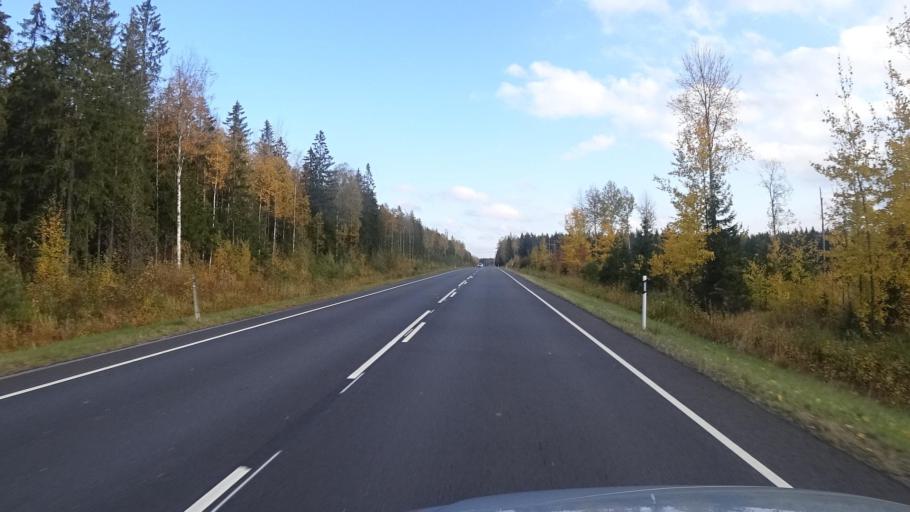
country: FI
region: Satakunta
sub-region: Rauma
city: Eura
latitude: 61.1148
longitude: 22.1962
